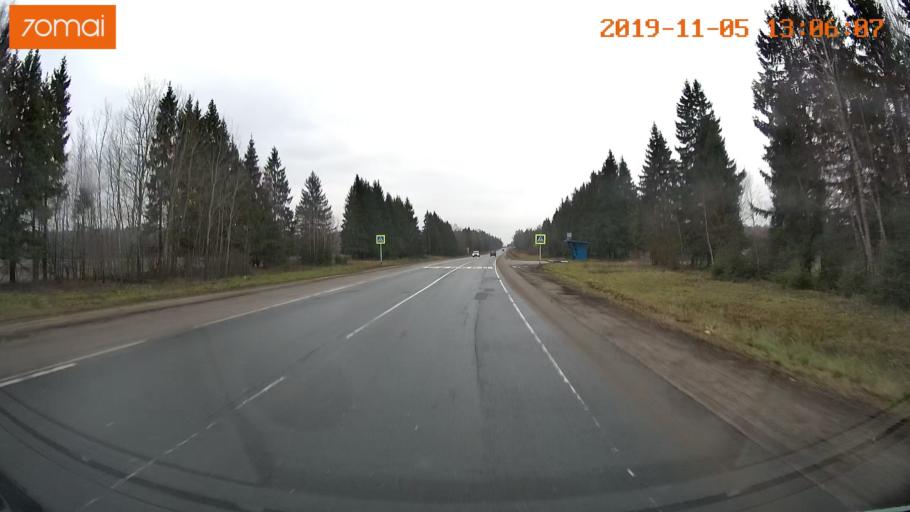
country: RU
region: Ivanovo
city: Kitovo
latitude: 56.8781
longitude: 41.2575
